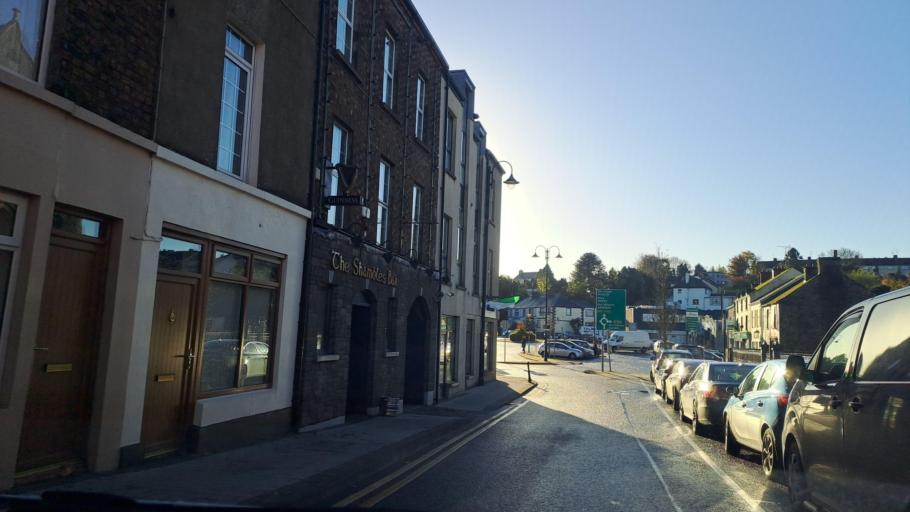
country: IE
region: Ulster
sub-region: County Monaghan
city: Monaghan
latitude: 54.2476
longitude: -6.9663
